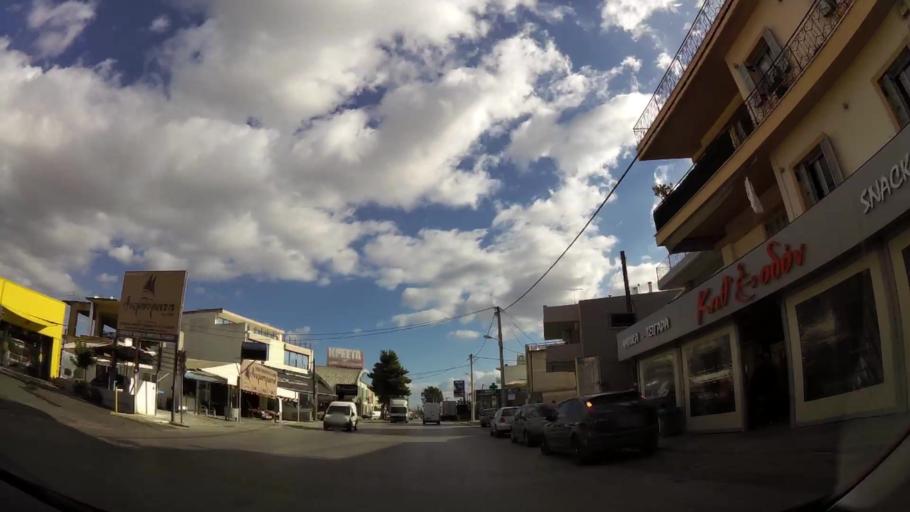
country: GR
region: Attica
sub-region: Nomarchia Anatolikis Attikis
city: Acharnes
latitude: 38.0843
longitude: 23.7459
